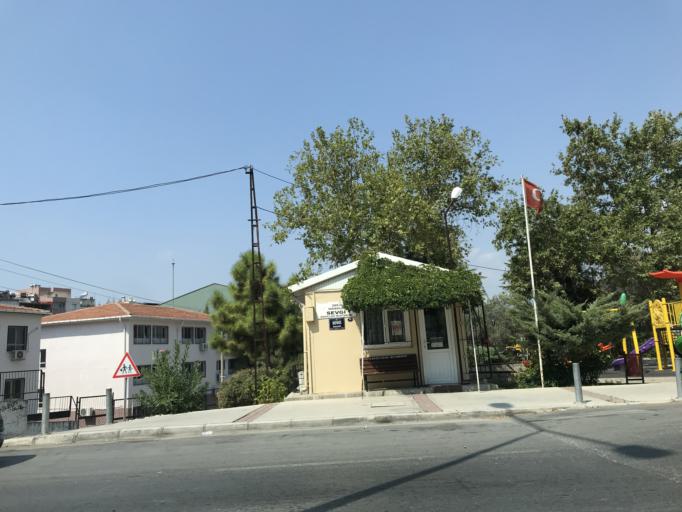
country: TR
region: Izmir
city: Karabaglar
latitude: 38.3839
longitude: 27.1152
